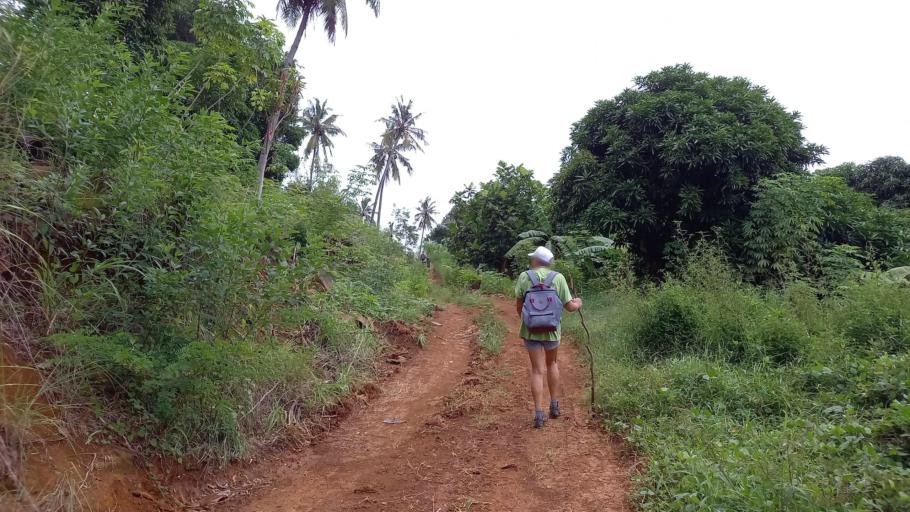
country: YT
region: Acoua
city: Acoua
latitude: -12.7125
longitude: 45.0539
